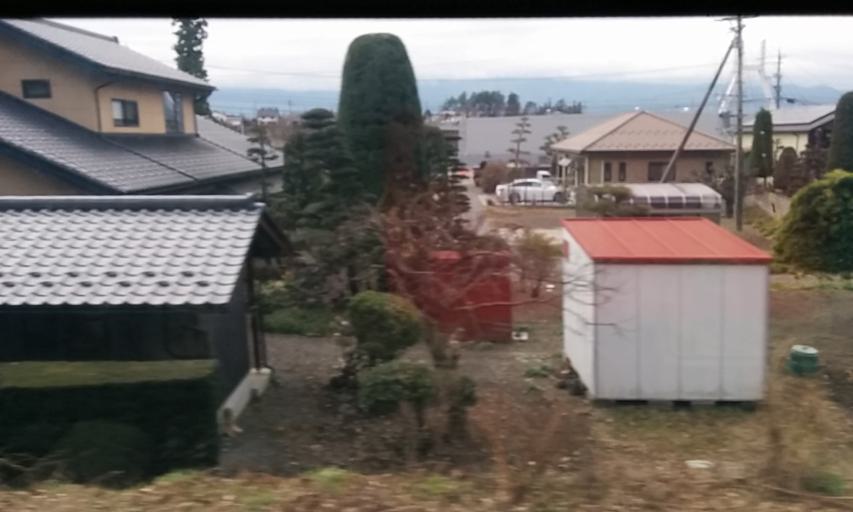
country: JP
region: Nagano
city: Matsumoto
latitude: 36.2650
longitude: 137.9479
